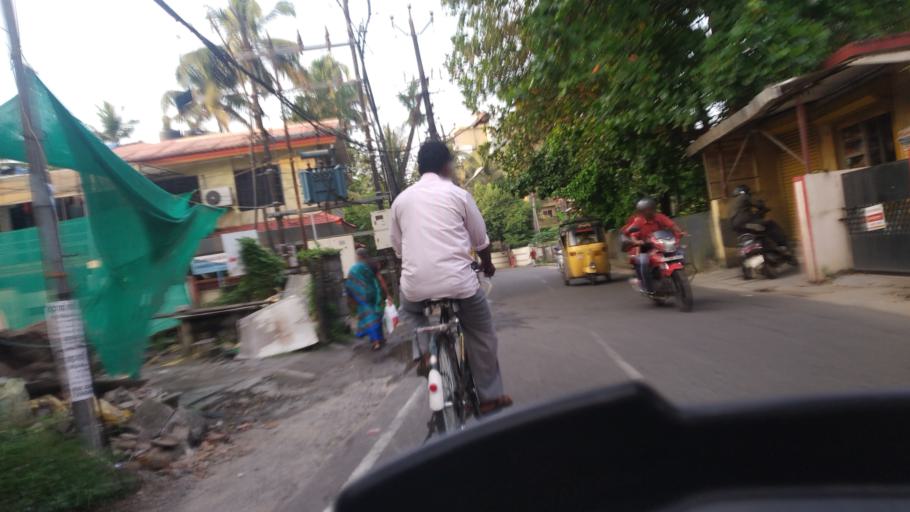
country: IN
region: Kerala
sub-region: Ernakulam
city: Elur
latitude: 10.0258
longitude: 76.2985
